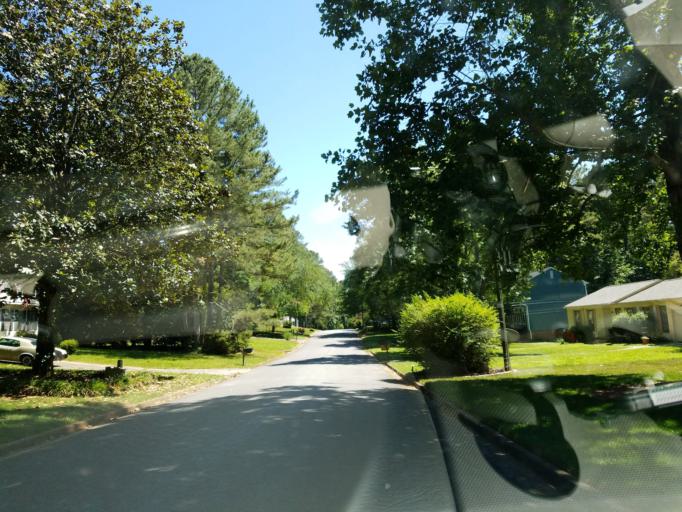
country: US
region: Georgia
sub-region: Cobb County
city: Marietta
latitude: 33.9624
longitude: -84.4683
